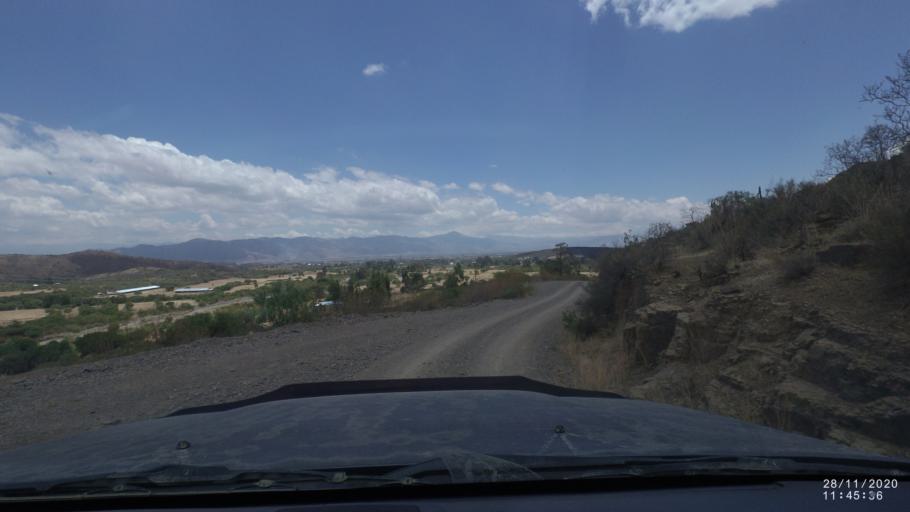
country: BO
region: Cochabamba
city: Tarata
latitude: -17.6538
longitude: -66.0452
